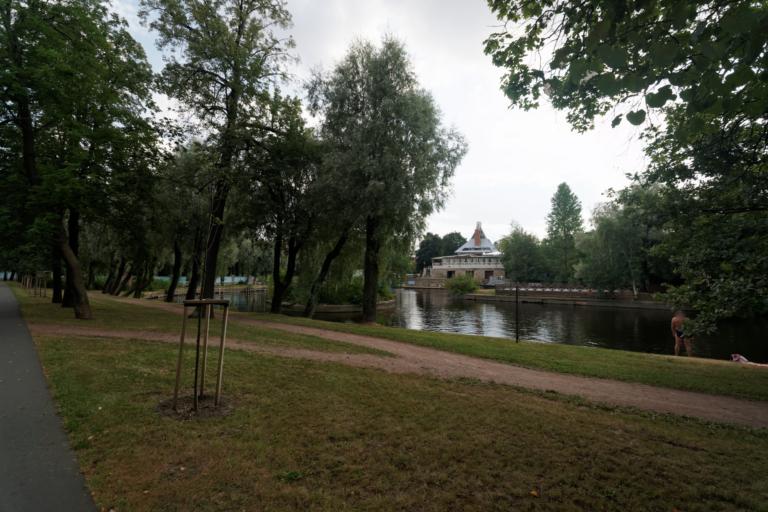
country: RU
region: St.-Petersburg
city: Novaya Derevnya
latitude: 59.9756
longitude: 30.2786
